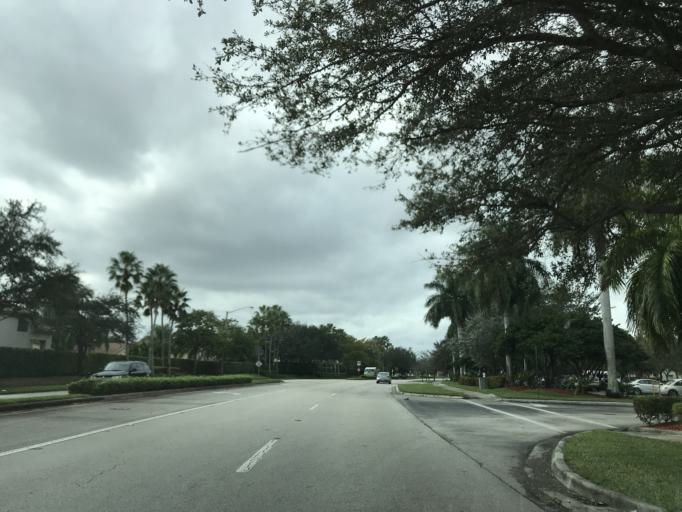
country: US
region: Florida
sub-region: Broward County
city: Coral Springs
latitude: 26.2976
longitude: -80.2762
